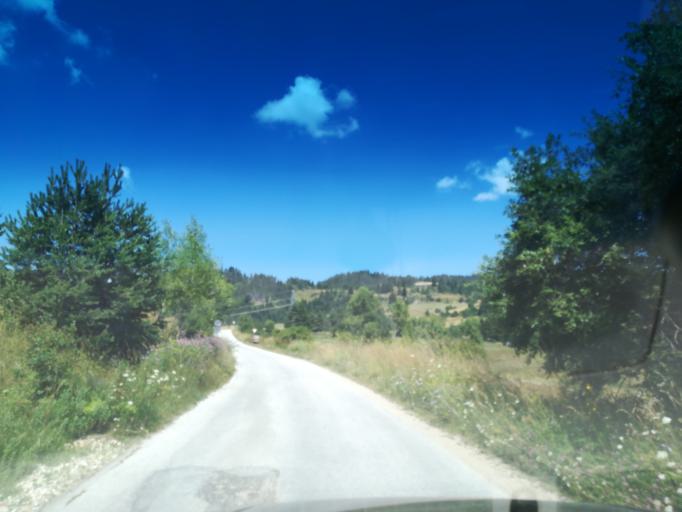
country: BG
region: Smolyan
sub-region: Obshtina Chepelare
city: Chepelare
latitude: 41.6694
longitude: 24.7793
